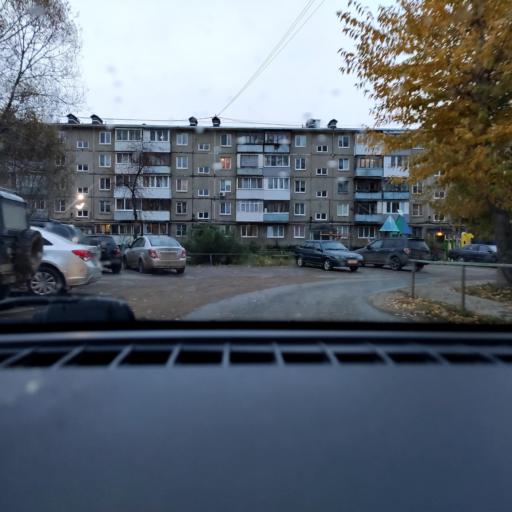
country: RU
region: Perm
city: Perm
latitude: 57.9642
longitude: 56.1854
